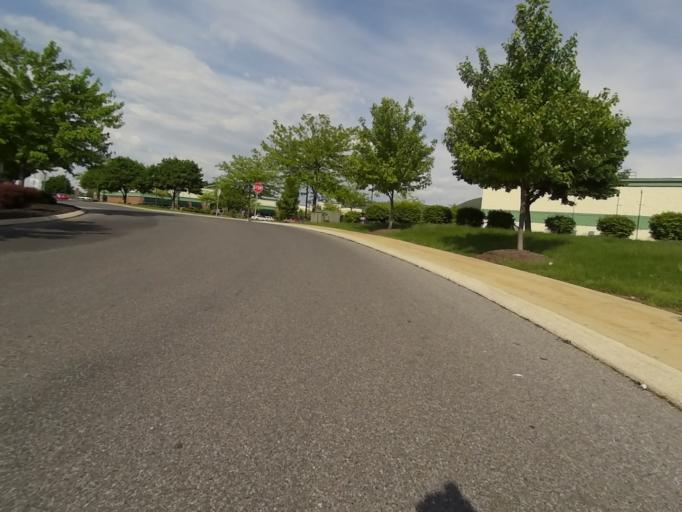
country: US
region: Pennsylvania
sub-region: Centre County
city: Lemont
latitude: 40.8304
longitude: -77.8066
